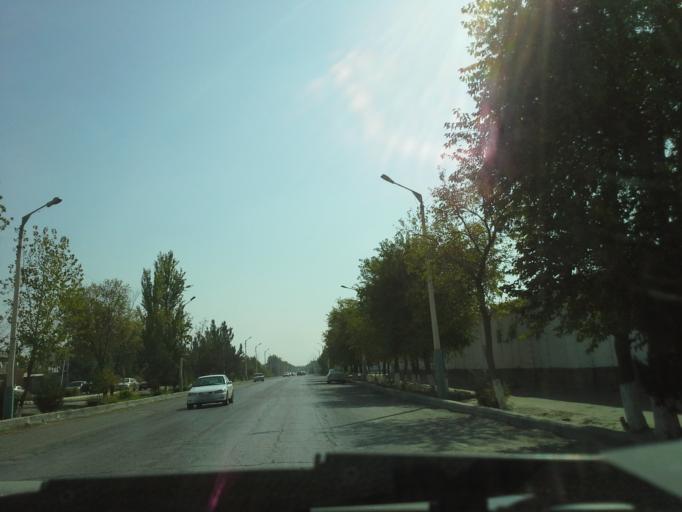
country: TM
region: Lebap
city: Atamyrat
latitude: 37.8416
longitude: 65.2036
